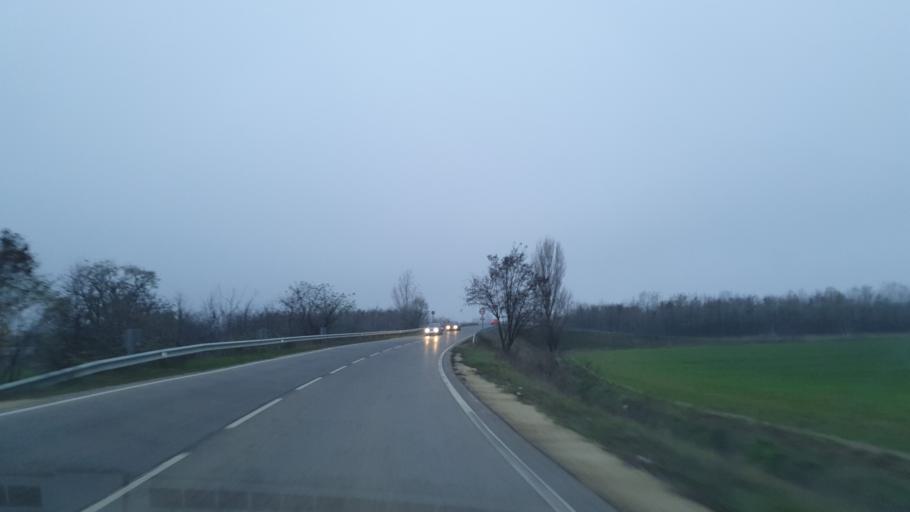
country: HU
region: Pest
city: Csomor
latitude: 47.5370
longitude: 19.2227
